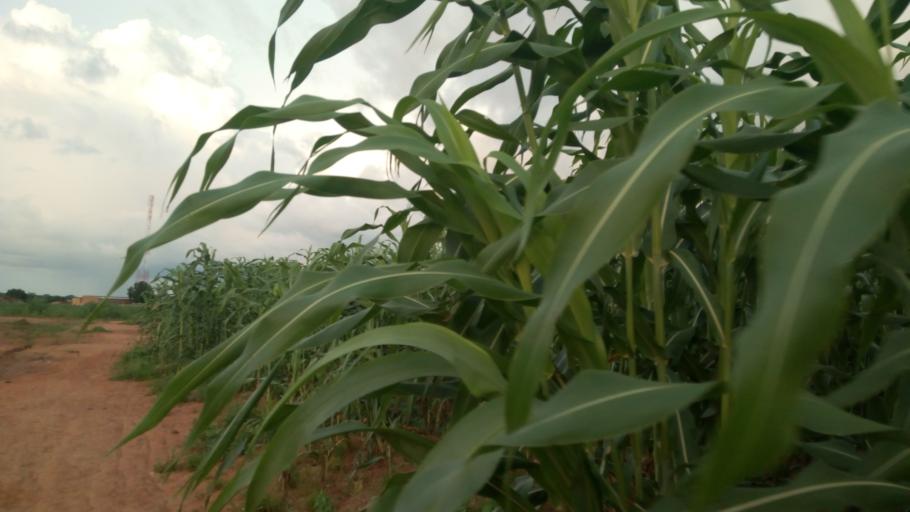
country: ML
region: Sikasso
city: Koutiala
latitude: 12.3778
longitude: -5.4978
